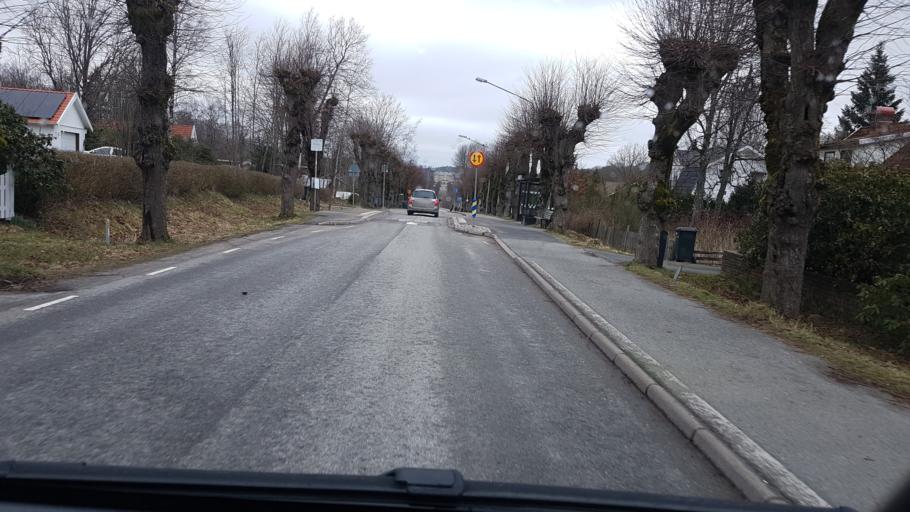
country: SE
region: Vaestra Goetaland
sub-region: Lerums Kommun
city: Stenkullen
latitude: 57.7994
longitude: 12.3698
